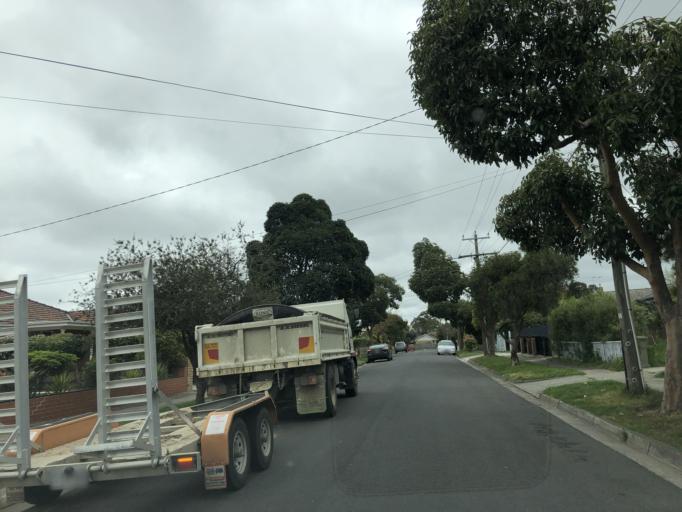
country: AU
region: Victoria
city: Burwood East
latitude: -37.8573
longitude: 145.1449
